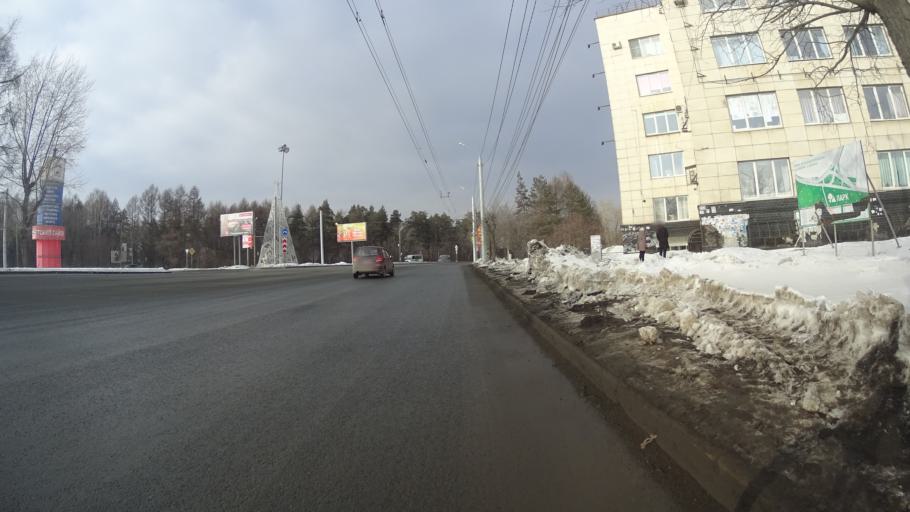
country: RU
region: Chelyabinsk
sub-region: Gorod Chelyabinsk
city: Chelyabinsk
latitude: 55.1277
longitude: 61.3665
